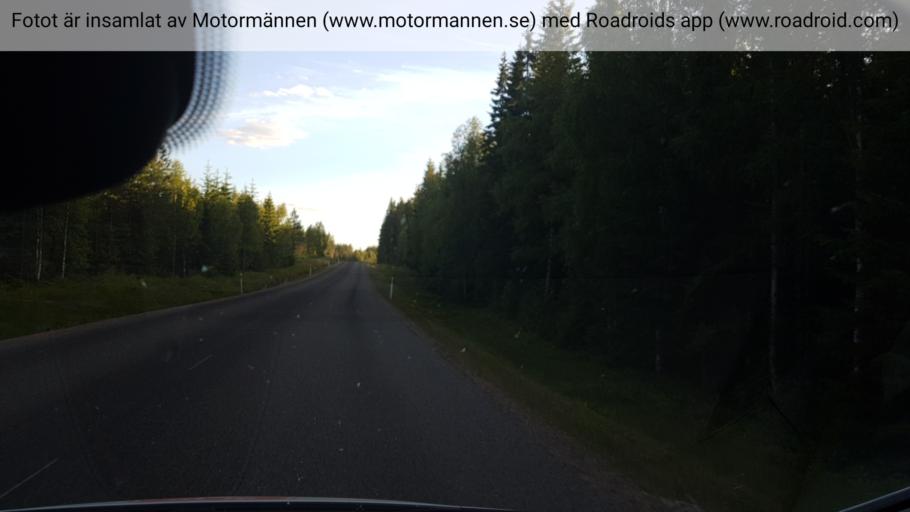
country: SE
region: Vaermland
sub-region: Torsby Kommun
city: Torsby
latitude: 60.3488
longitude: 13.1672
